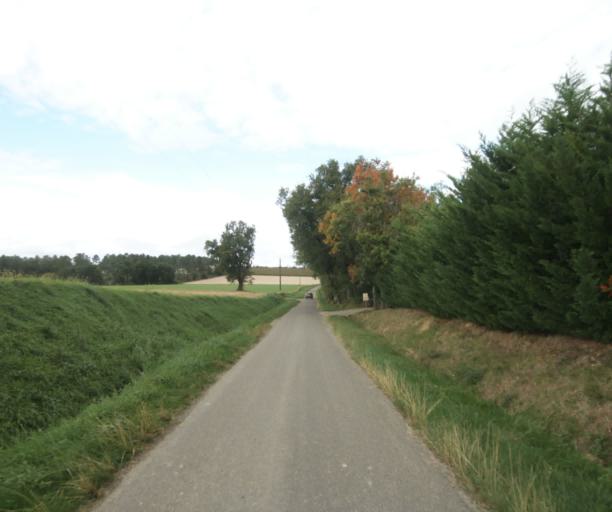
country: FR
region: Midi-Pyrenees
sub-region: Departement du Gers
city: Eauze
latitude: 43.9165
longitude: 0.1207
